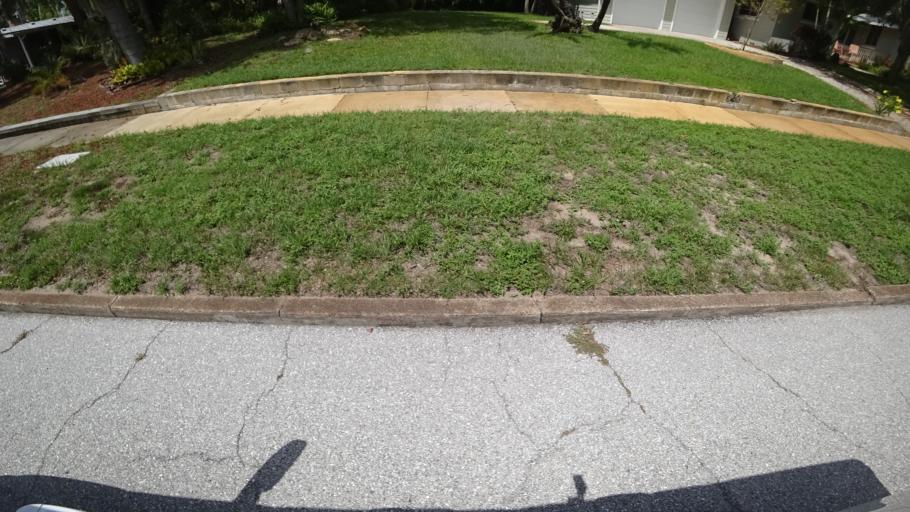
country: US
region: Florida
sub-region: Manatee County
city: Whitfield
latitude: 27.4087
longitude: -82.5738
